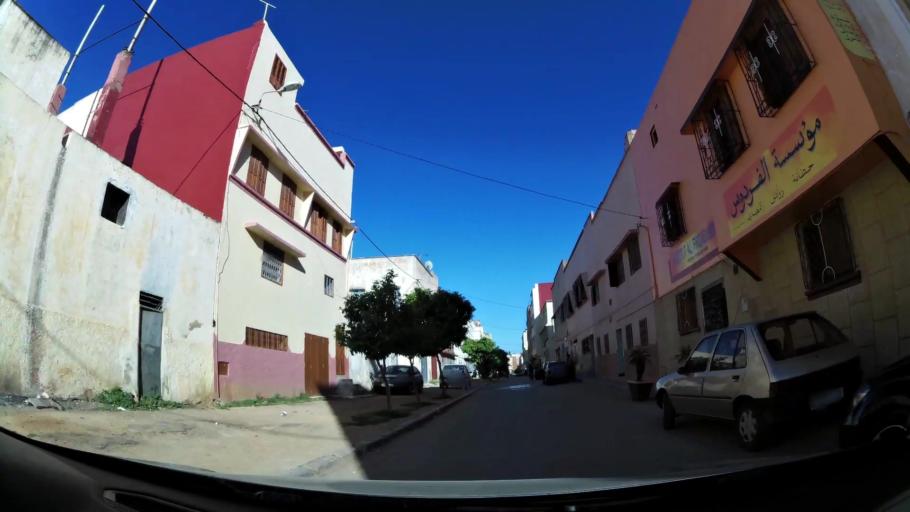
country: MA
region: Meknes-Tafilalet
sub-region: Meknes
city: Meknes
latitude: 33.8796
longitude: -5.5649
